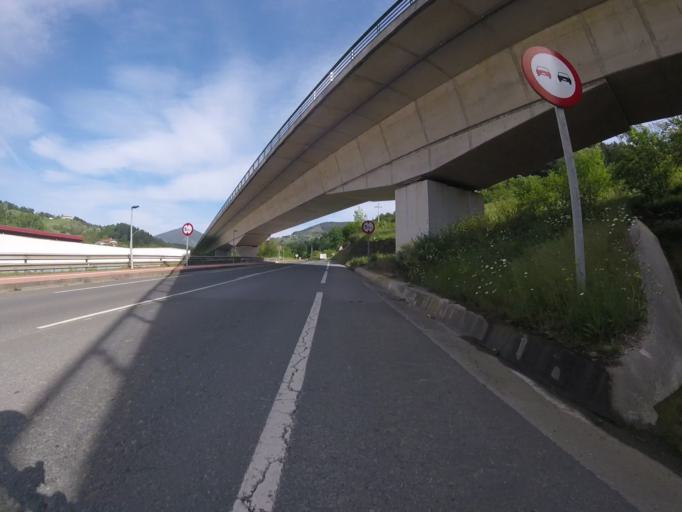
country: ES
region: Basque Country
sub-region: Provincia de Guipuzcoa
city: Gabiria
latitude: 43.0736
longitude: -2.2888
